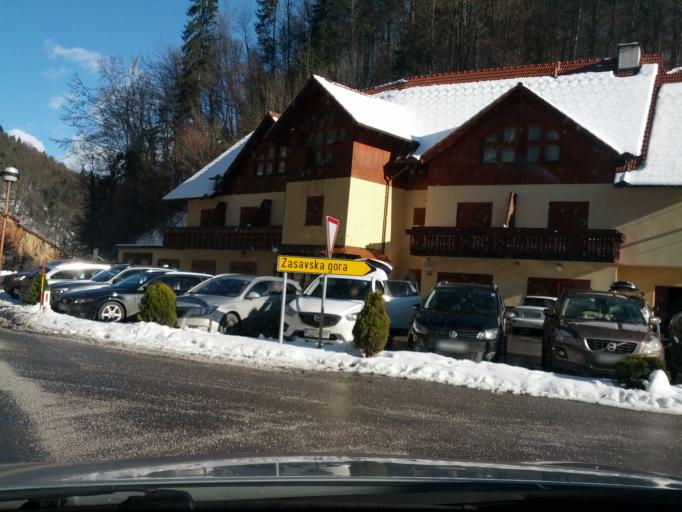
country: SI
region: Zagorje ob Savi
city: Izlake
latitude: 46.1365
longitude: 14.8640
